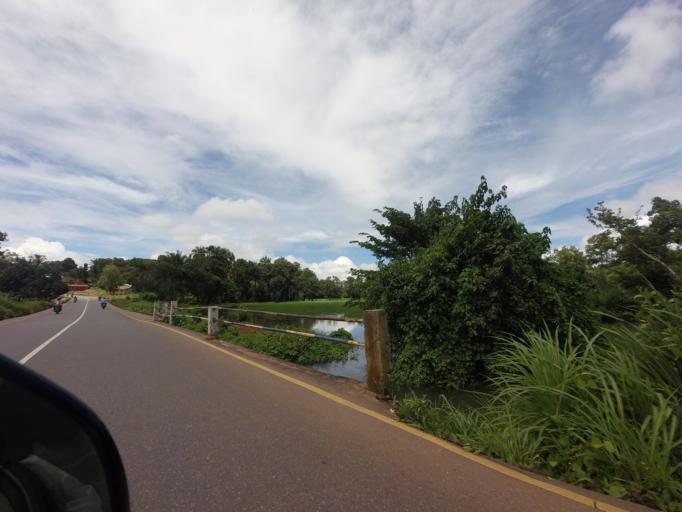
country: SL
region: Northern Province
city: Kambia
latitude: 9.1185
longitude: -12.9202
